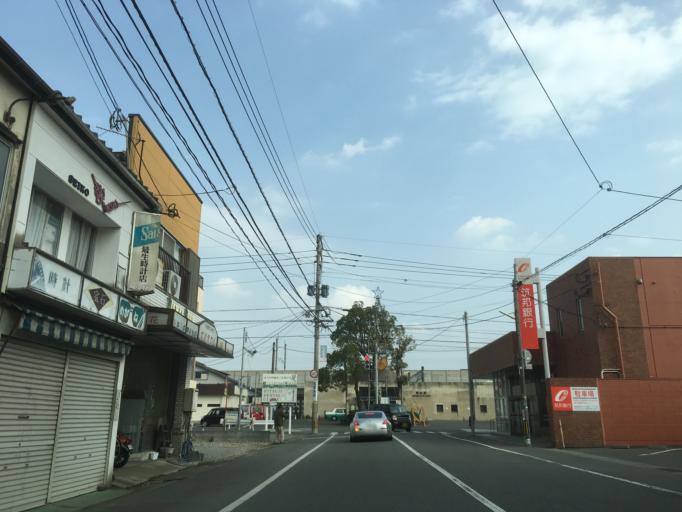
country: JP
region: Fukuoka
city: Kurume
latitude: 33.2762
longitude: 130.5016
